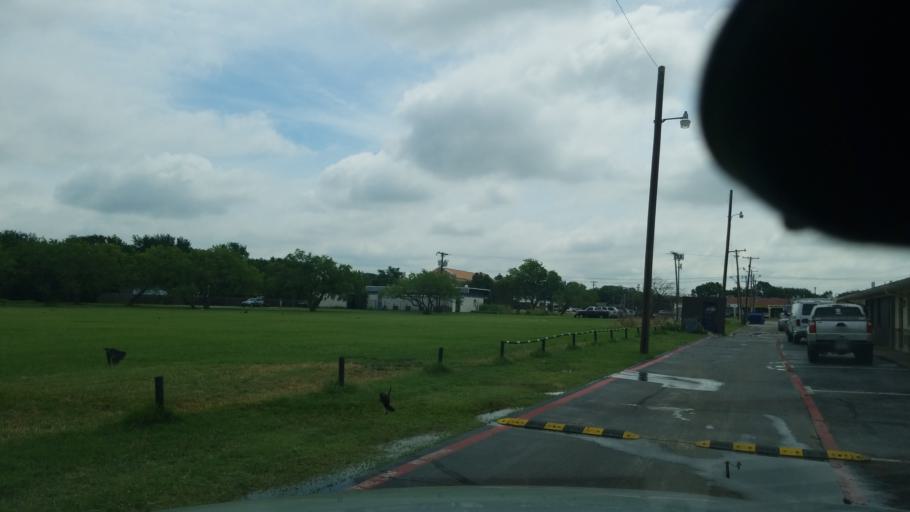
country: US
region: Texas
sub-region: Dallas County
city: Irving
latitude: 32.8451
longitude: -96.9614
